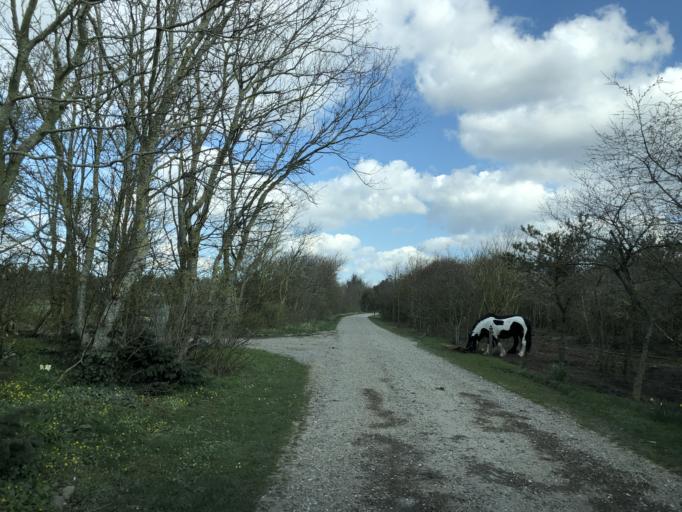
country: DK
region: Central Jutland
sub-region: Holstebro Kommune
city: Ulfborg
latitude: 56.3824
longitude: 8.2096
